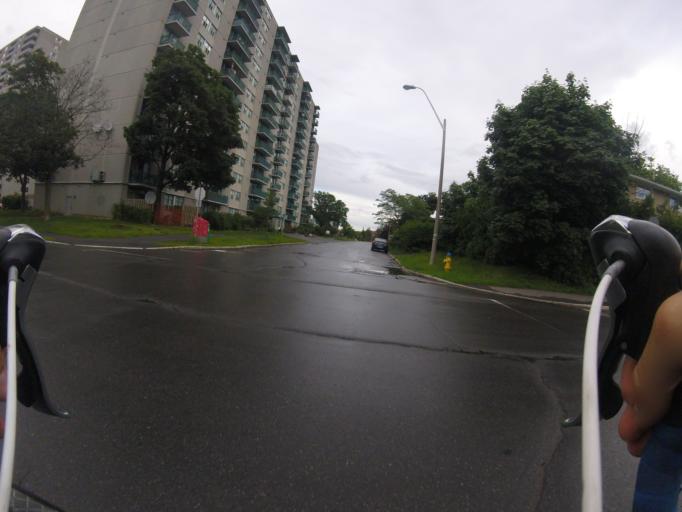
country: CA
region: Ontario
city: Bells Corners
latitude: 45.3652
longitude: -75.7932
